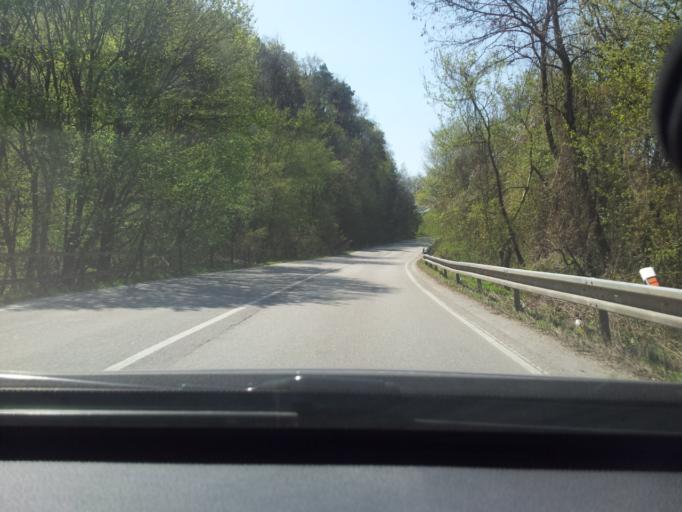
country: SK
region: Nitriansky
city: Zlate Moravce
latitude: 48.4908
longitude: 18.4217
